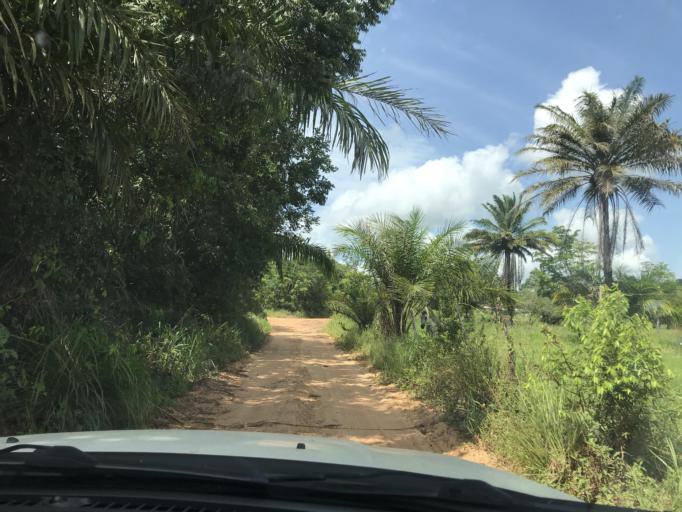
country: BR
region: Bahia
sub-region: Entre Rios
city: Entre Rios
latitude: -12.2186
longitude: -38.0802
